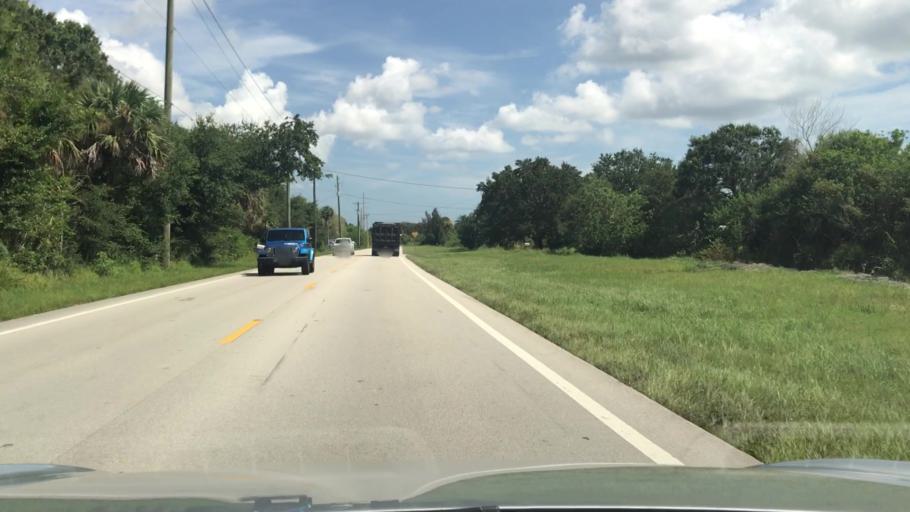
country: US
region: Florida
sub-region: Indian River County
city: Winter Beach
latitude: 27.7306
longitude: -80.4624
